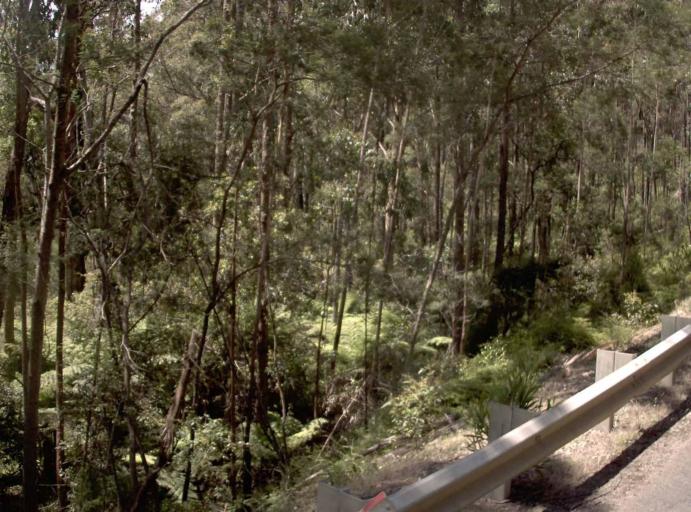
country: AU
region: New South Wales
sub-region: Bombala
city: Bombala
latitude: -37.5844
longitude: 149.0013
